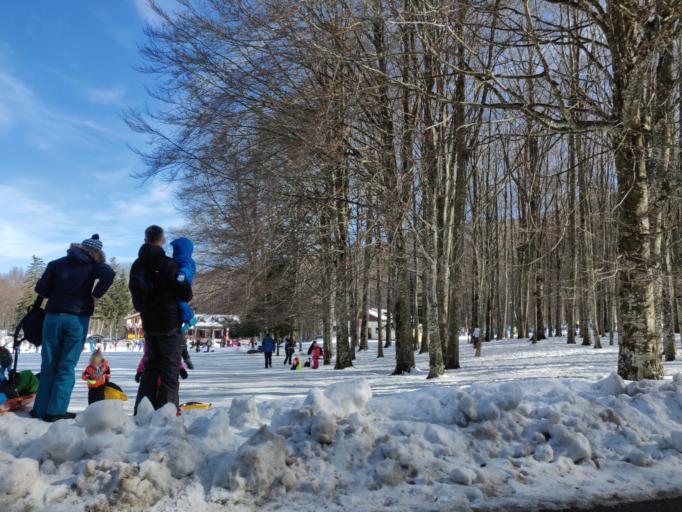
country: IT
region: Tuscany
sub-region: Provincia di Grosseto
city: Seggiano
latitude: 42.8904
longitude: 11.6052
